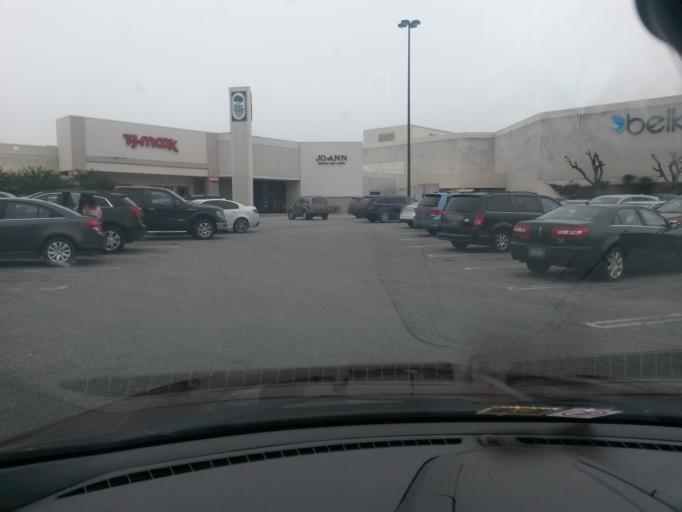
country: US
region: Virginia
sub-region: City of Lynchburg
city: West Lynchburg
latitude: 37.3665
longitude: -79.1784
